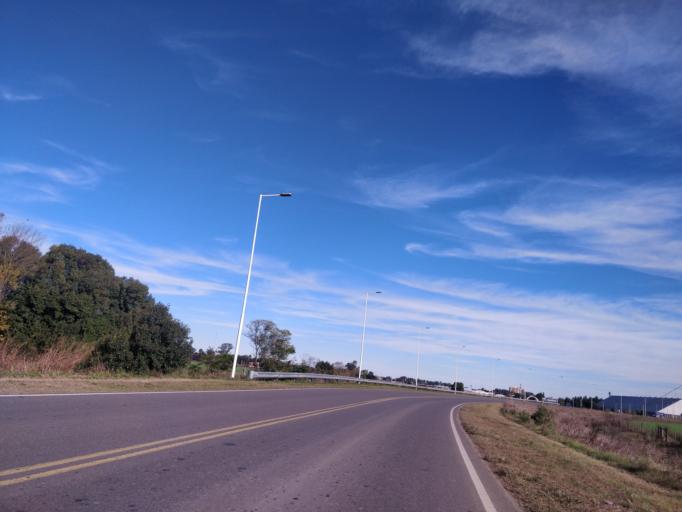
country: AR
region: Cordoba
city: Leones
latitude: -32.6459
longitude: -62.2912
